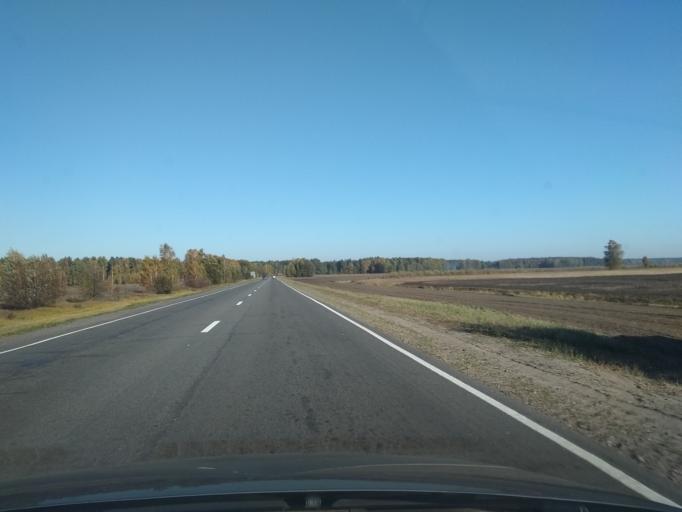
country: BY
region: Brest
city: Malaryta
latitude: 52.0019
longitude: 24.2144
